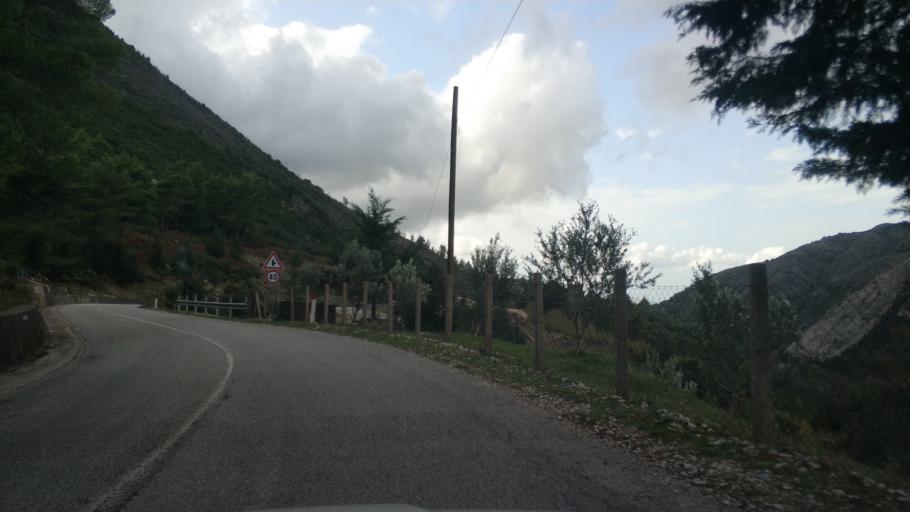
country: AL
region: Vlore
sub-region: Rrethi i Vlores
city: Orikum
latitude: 40.2466
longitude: 19.5481
